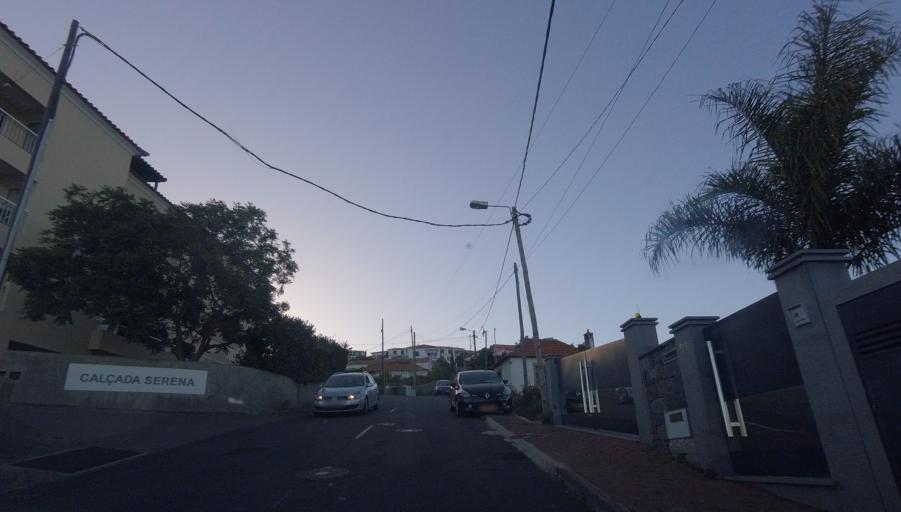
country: PT
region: Madeira
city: Canico
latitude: 32.6461
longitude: -16.8390
